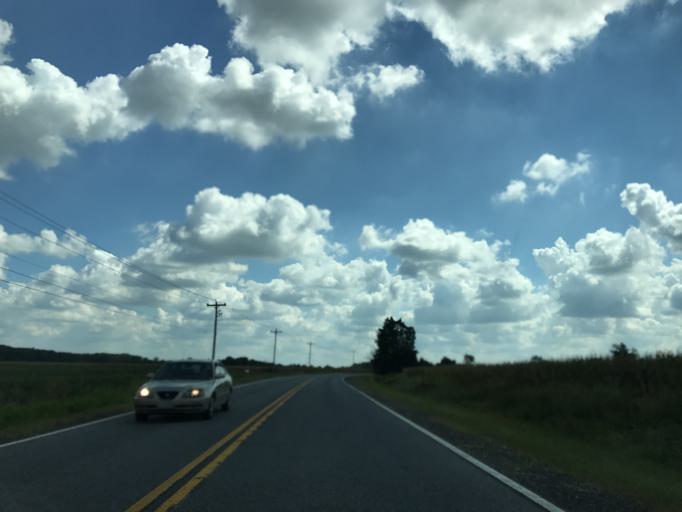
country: US
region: Maryland
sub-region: Queen Anne's County
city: Centreville
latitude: 39.0131
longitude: -75.9969
